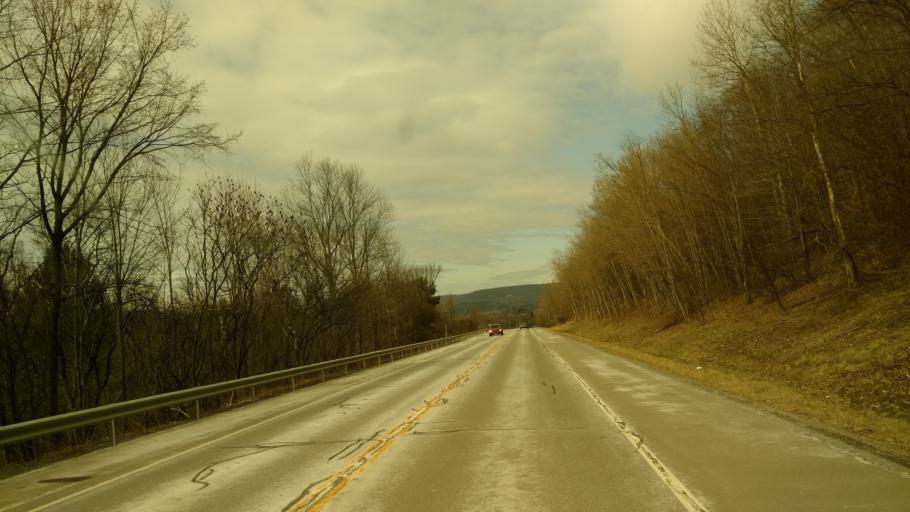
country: US
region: New York
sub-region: Allegany County
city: Wellsville
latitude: 42.0715
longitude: -77.9192
